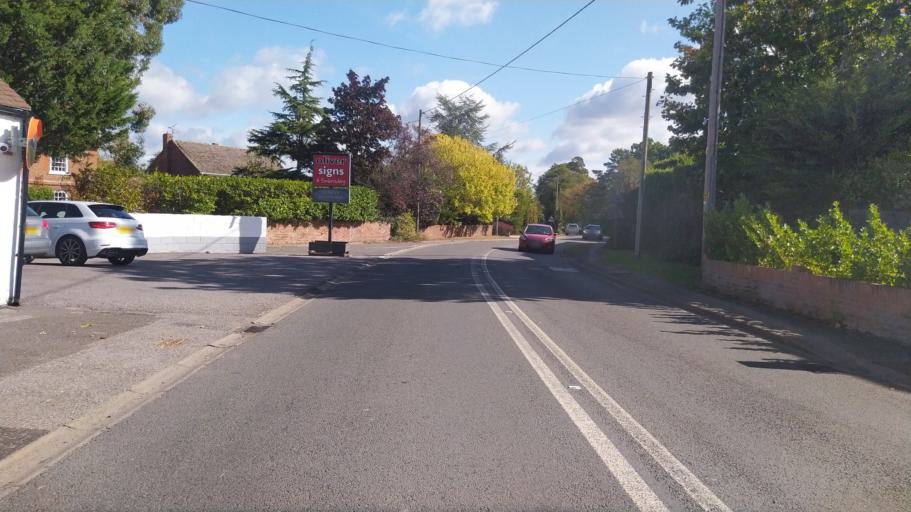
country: GB
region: England
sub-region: West Berkshire
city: Calcot
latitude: 51.4117
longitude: -1.0412
